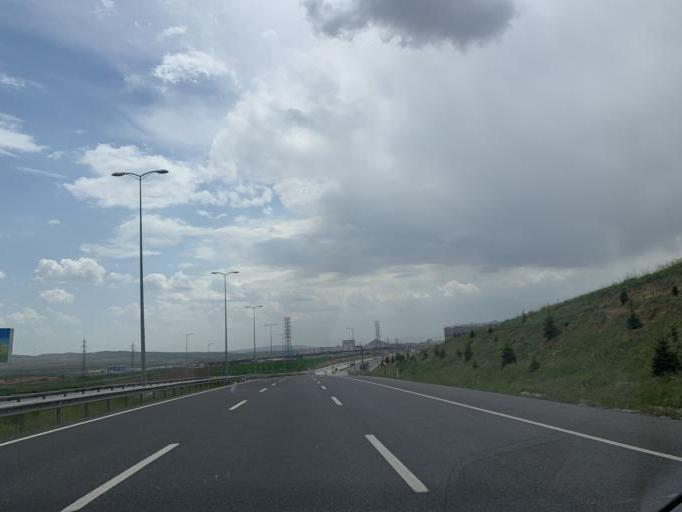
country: TR
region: Ankara
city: Polatli
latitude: 39.5927
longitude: 32.1729
